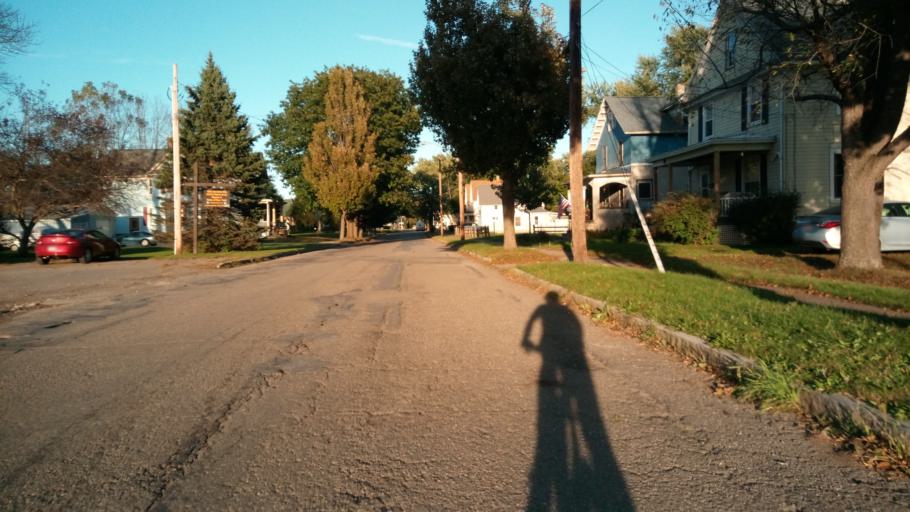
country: US
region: New York
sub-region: Chemung County
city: Elmira
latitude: 42.0803
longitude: -76.8178
